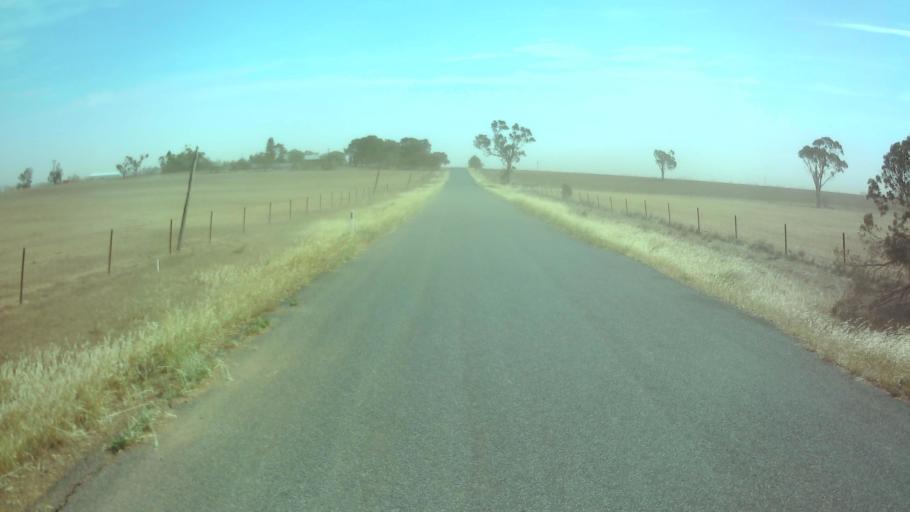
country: AU
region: New South Wales
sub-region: Weddin
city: Grenfell
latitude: -33.7338
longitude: 147.9975
